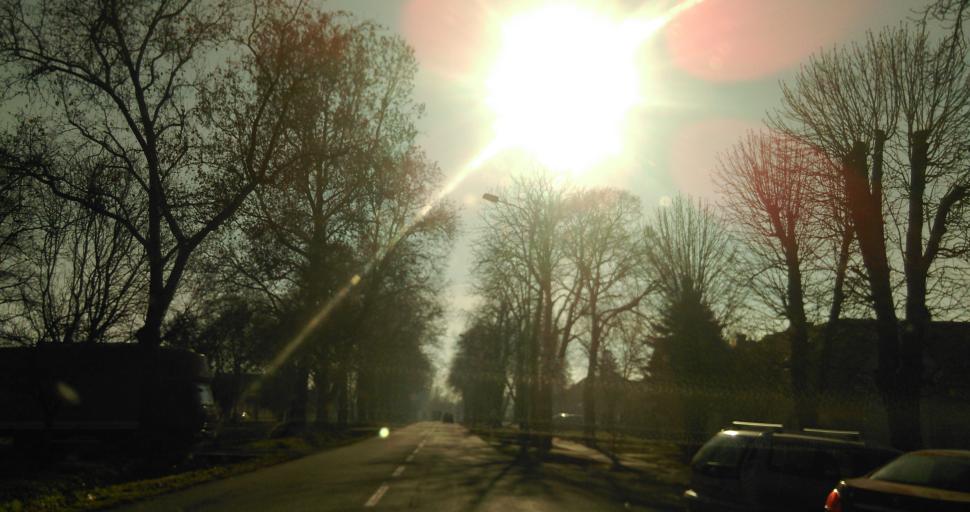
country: RS
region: Autonomna Pokrajina Vojvodina
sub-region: Sremski Okrug
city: Ruma
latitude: 44.9981
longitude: 19.8234
